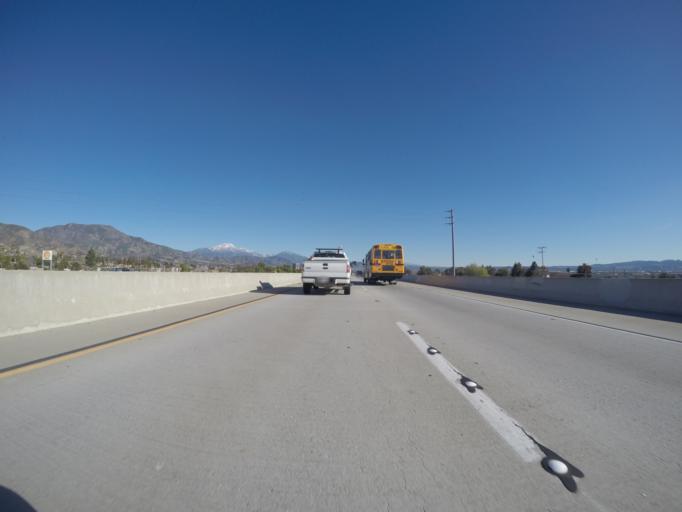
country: US
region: California
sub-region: San Bernardino County
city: Highland
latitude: 34.1358
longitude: -117.2363
